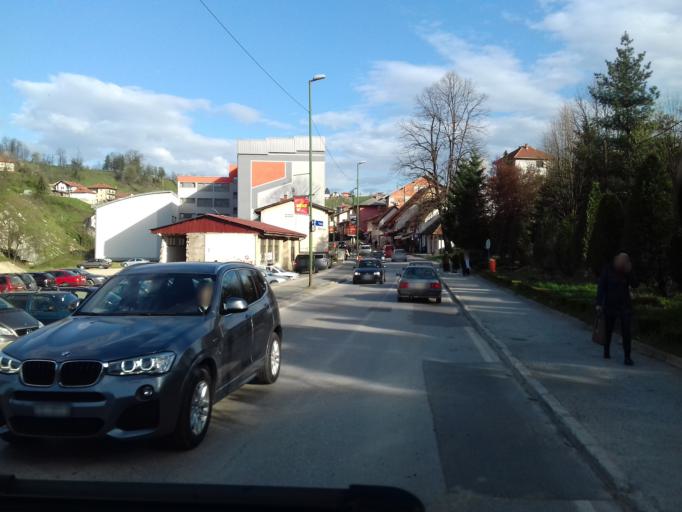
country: BA
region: Federation of Bosnia and Herzegovina
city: Tesanj
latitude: 44.6099
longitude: 17.9883
